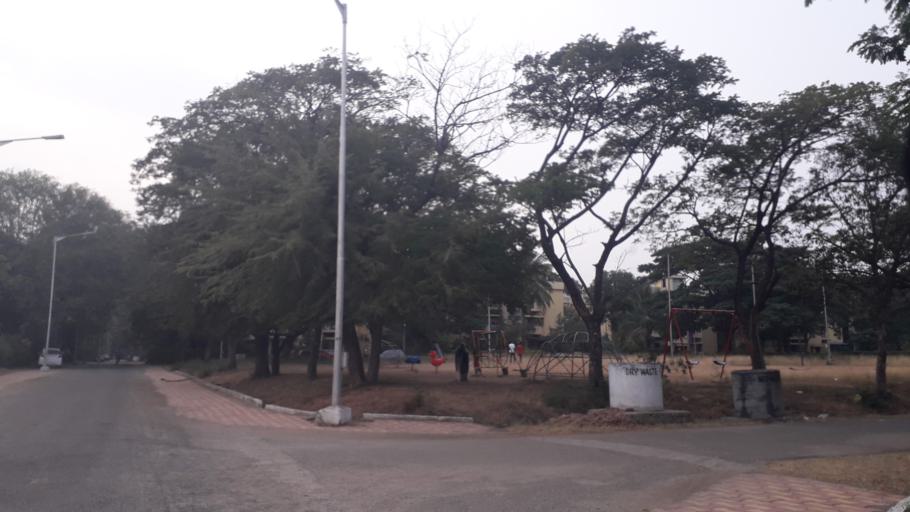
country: IN
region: Telangana
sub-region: Rangareddi
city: Singapur
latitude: 17.4656
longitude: 78.1643
